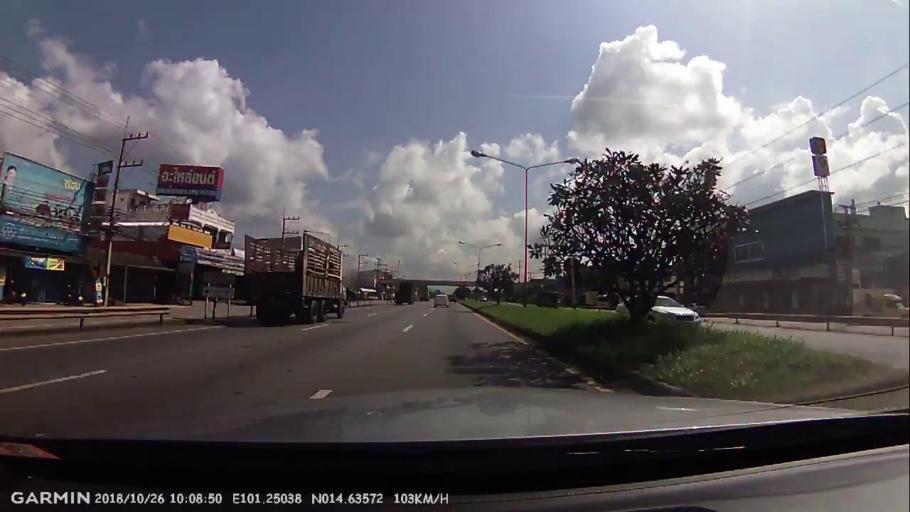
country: TH
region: Sara Buri
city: Muak Lek
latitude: 14.6358
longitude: 101.2508
